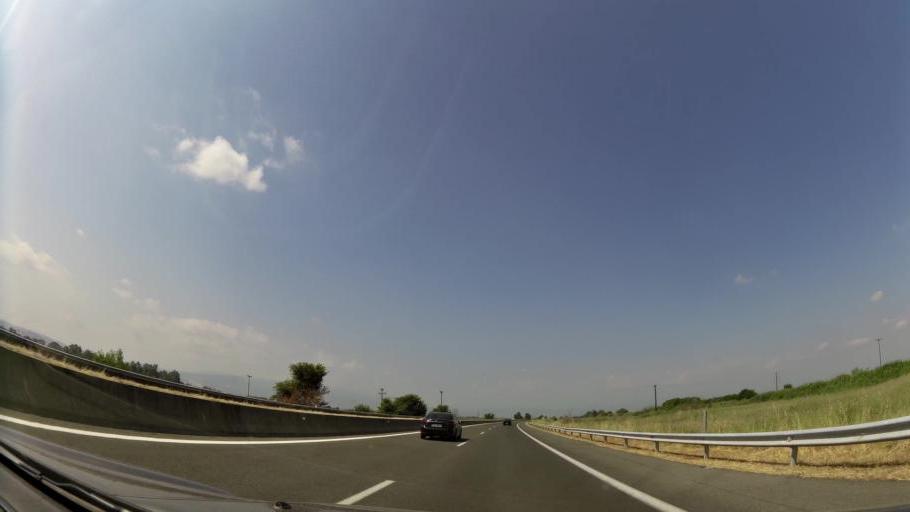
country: GR
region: Central Macedonia
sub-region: Nomos Imathias
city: Loutros
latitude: 40.5773
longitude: 22.4017
